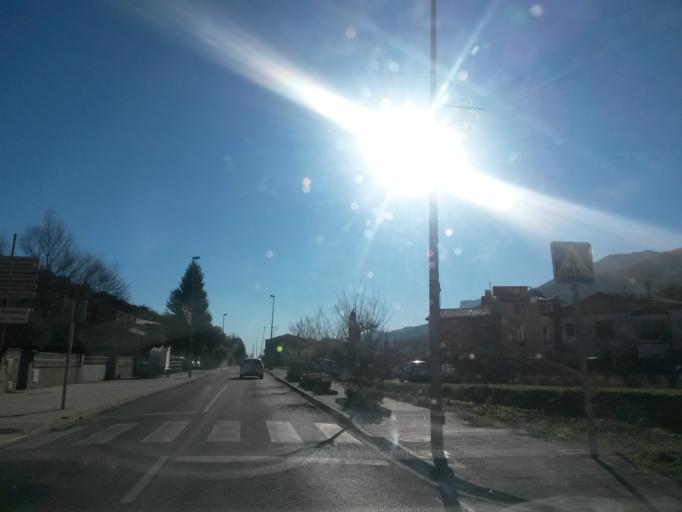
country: ES
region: Catalonia
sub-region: Provincia de Girona
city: Sant Feliu de Pallerols
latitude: 42.0780
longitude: 2.5102
